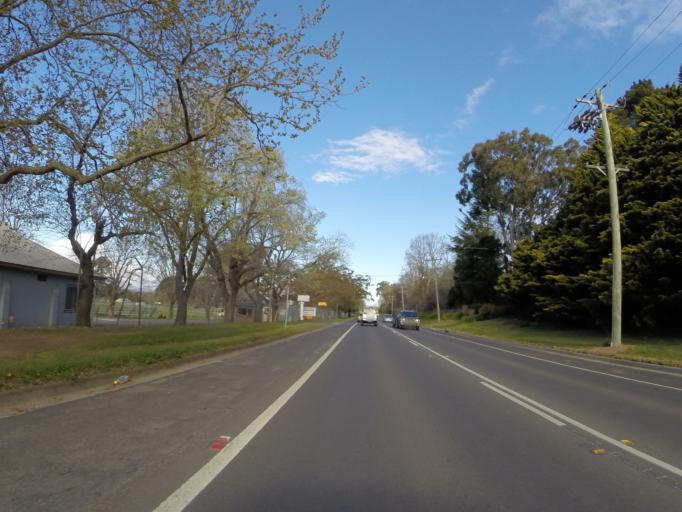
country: AU
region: New South Wales
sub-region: Wingecarribee
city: Moss Vale
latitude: -34.5477
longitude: 150.3810
